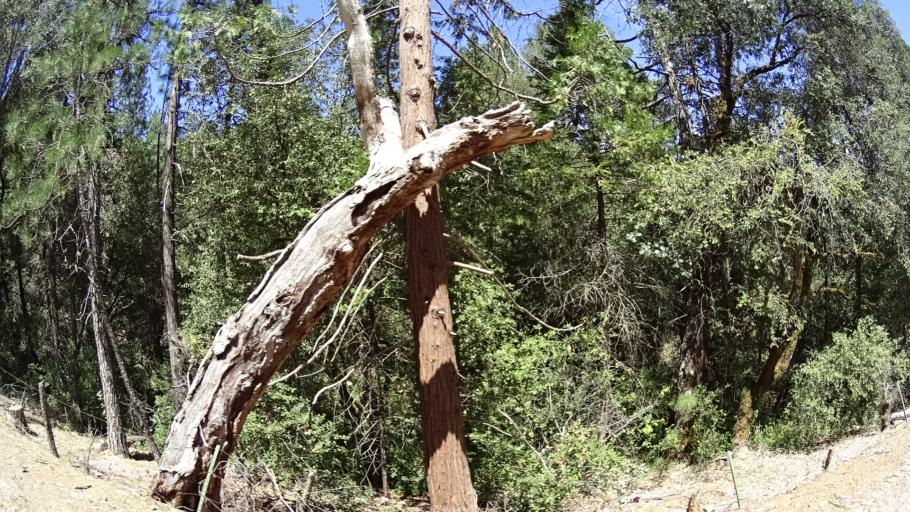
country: US
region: California
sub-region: Calaveras County
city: Forest Meadows
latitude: 38.2159
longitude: -120.4391
